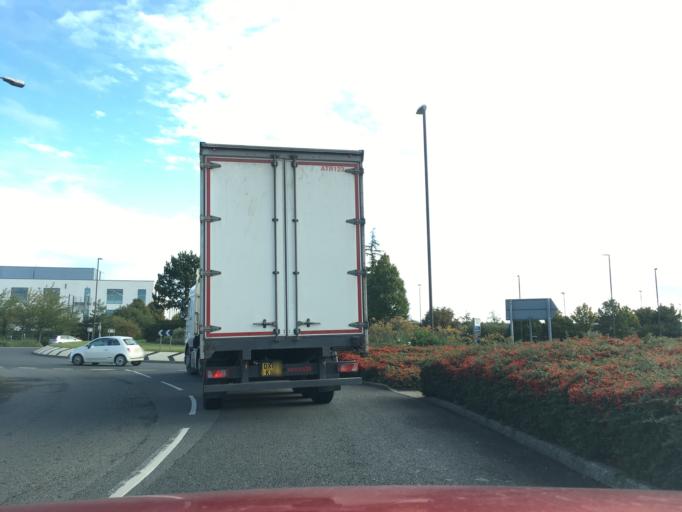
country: GB
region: England
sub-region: Gloucestershire
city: Barnwood
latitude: 51.8472
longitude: -2.1754
